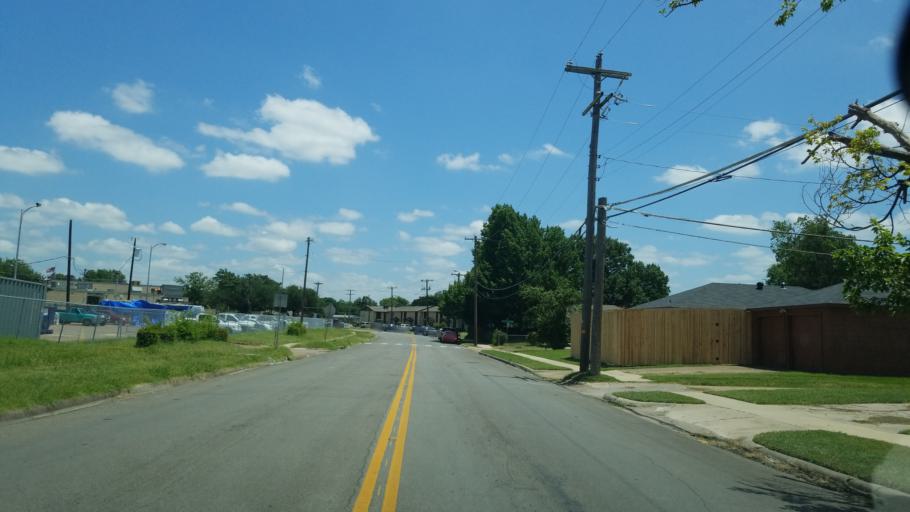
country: US
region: Texas
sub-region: Dallas County
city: Balch Springs
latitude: 32.7391
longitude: -96.7028
